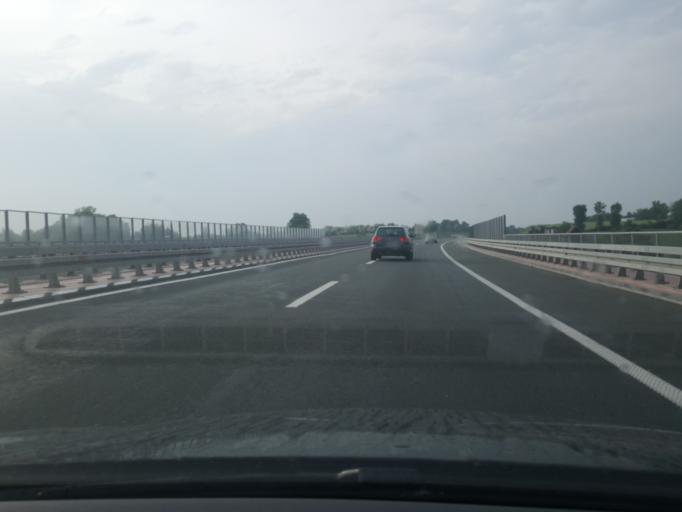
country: RS
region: Central Serbia
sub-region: Kolubarski Okrug
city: Lajkovac
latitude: 44.3639
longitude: 20.1228
